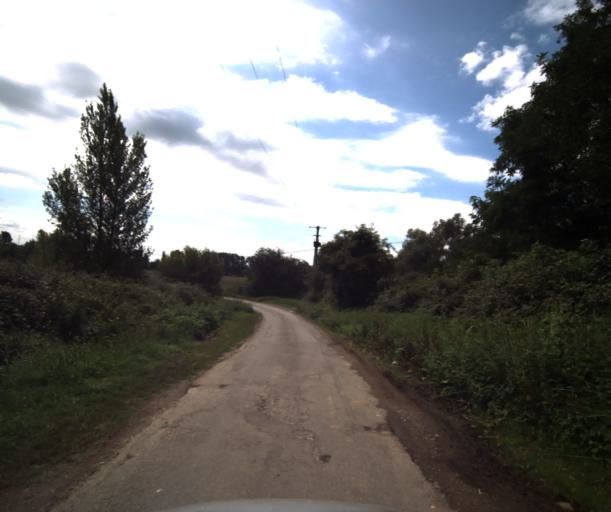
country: FR
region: Midi-Pyrenees
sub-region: Departement de la Haute-Garonne
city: Lacasse
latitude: 43.3791
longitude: 1.2559
